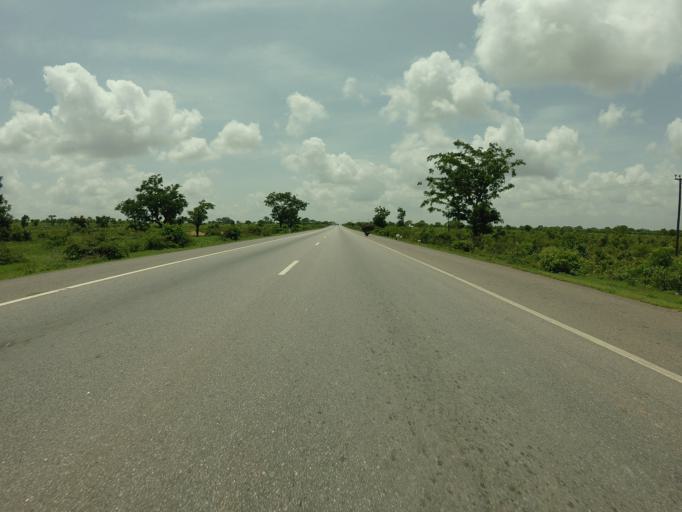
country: GH
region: Northern
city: Tamale
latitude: 9.2691
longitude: -1.0002
